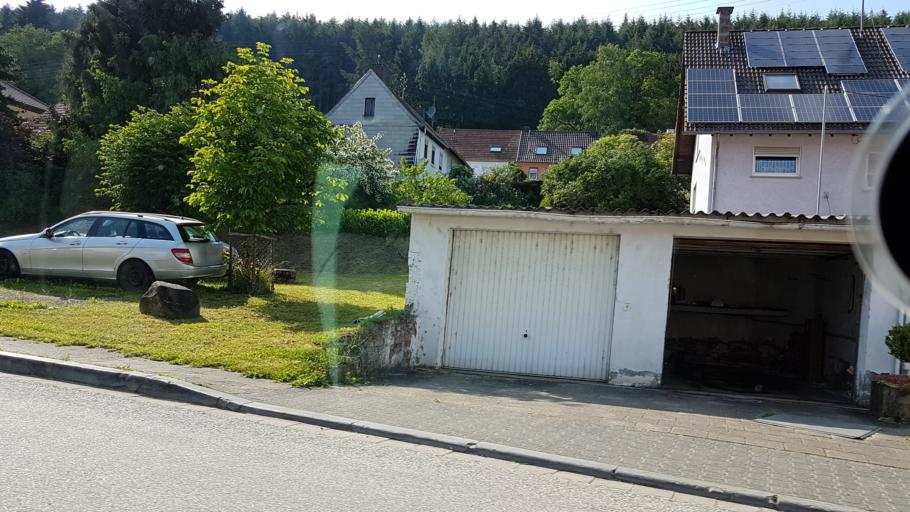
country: DE
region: Rheinland-Pfalz
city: Sankt Julian
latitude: 49.6086
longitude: 7.5120
